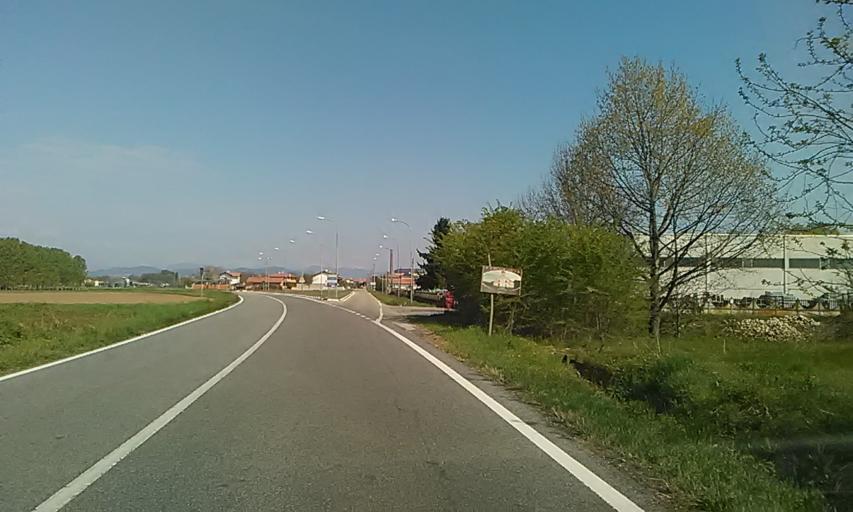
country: IT
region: Piedmont
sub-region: Provincia di Vercelli
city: Lenta
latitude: 45.5474
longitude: 8.3848
